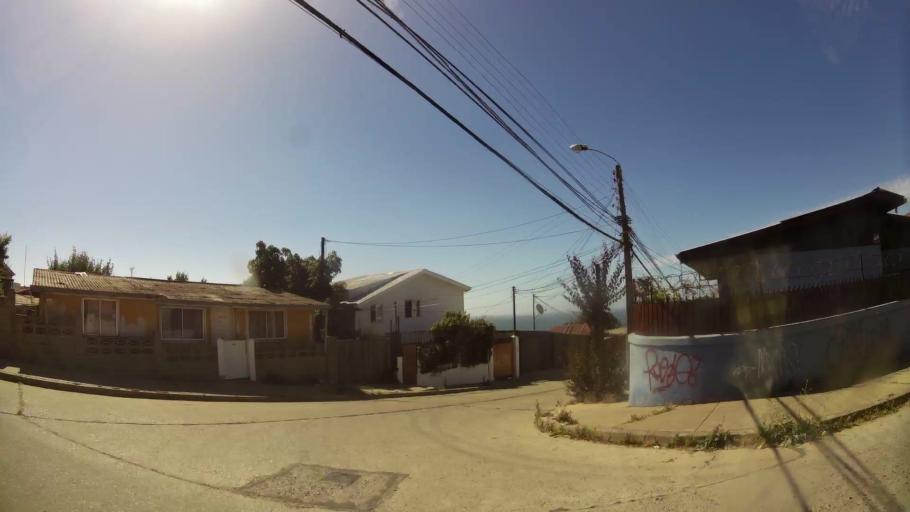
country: CL
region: Valparaiso
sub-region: Provincia de Valparaiso
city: Vina del Mar
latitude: -33.0325
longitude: -71.5750
